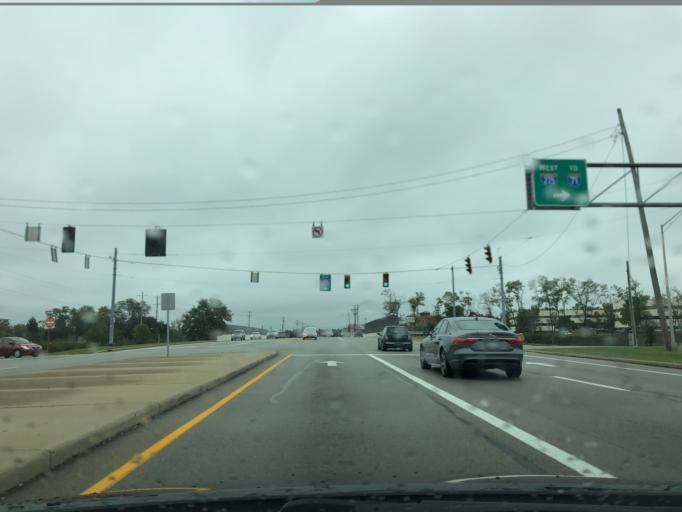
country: US
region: Ohio
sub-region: Hamilton County
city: Sixteen Mile Stand
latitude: 39.2626
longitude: -84.3368
